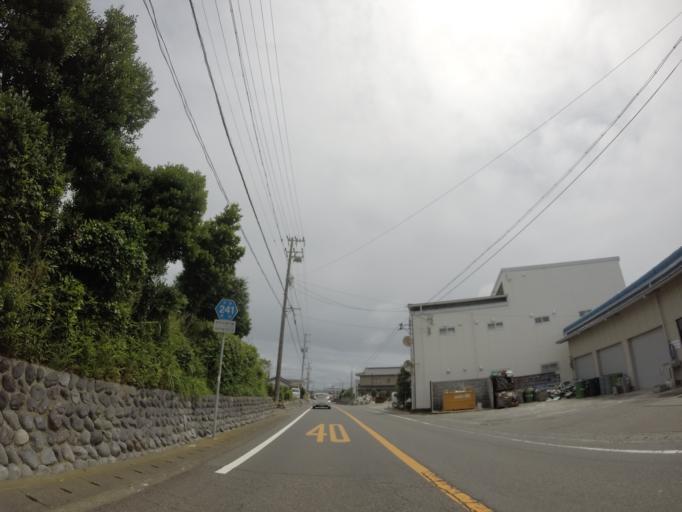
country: JP
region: Shizuoka
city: Oyama
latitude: 34.6187
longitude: 138.2013
